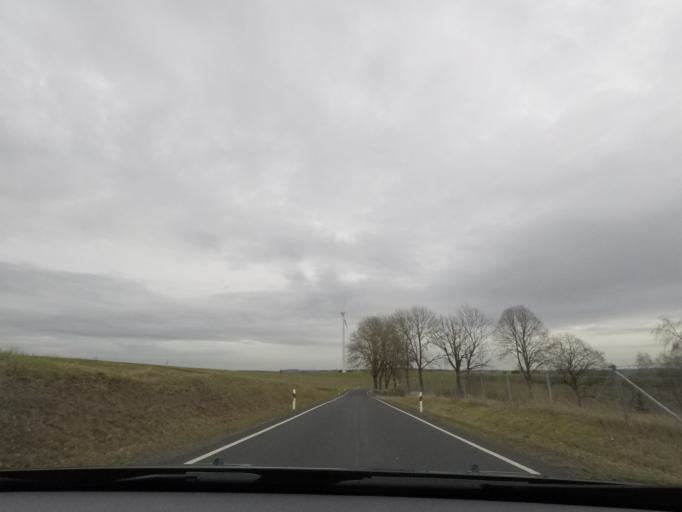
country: LU
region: Diekirch
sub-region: Canton de Clervaux
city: Wincrange
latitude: 50.0177
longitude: 5.8918
